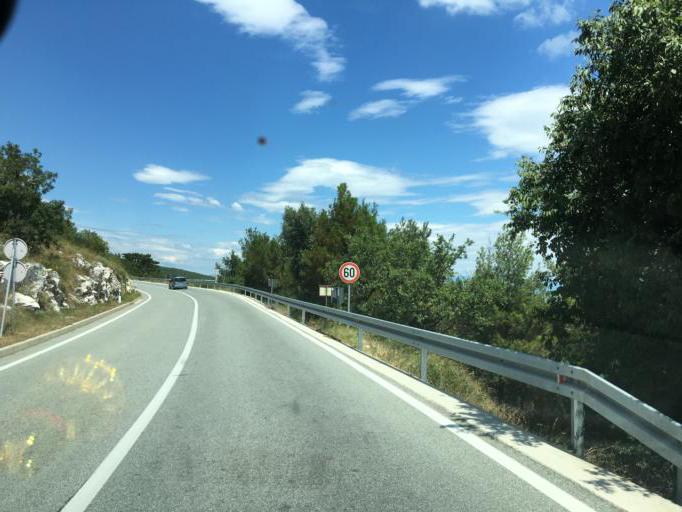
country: HR
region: Istarska
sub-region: Grad Labin
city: Rabac
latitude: 45.1224
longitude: 14.2045
